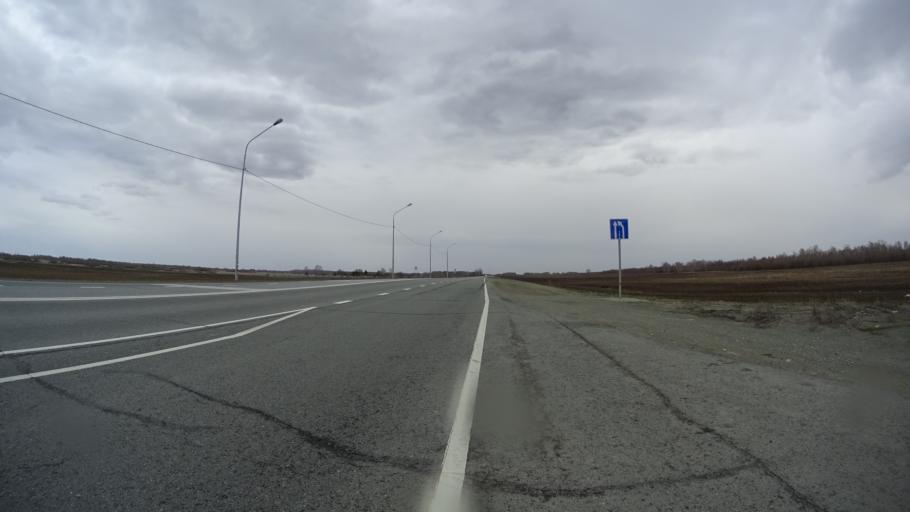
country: RU
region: Chelyabinsk
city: Krasnogorskiy
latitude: 54.6718
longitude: 61.2501
